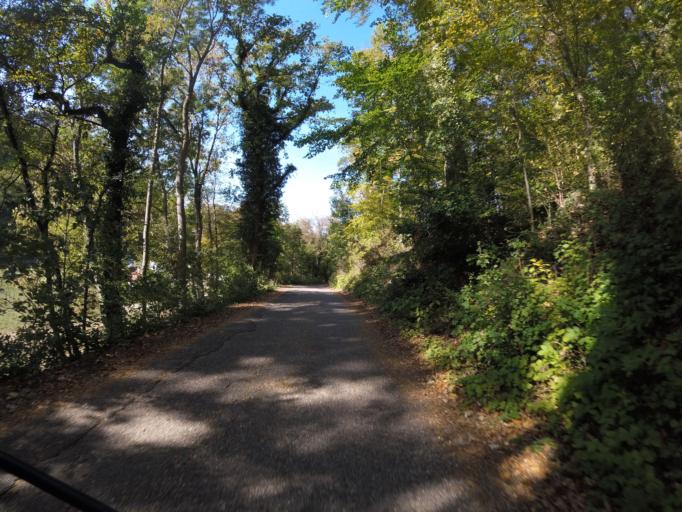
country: DE
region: Baden-Wuerttemberg
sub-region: Karlsruhe Region
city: Knittlingen
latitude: 49.0052
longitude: 8.7267
